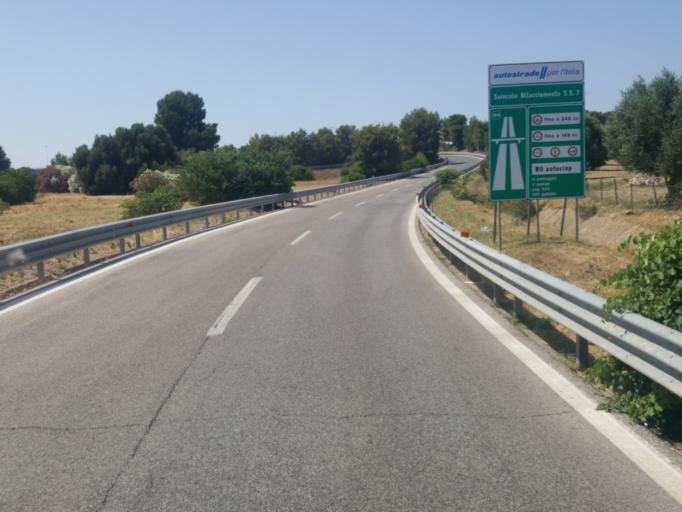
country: IT
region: Apulia
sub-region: Provincia di Taranto
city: Massafra
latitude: 40.5959
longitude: 17.0870
